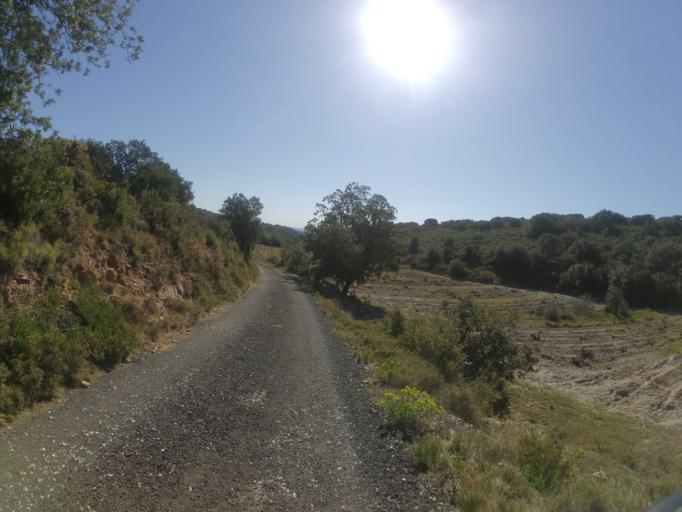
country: FR
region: Languedoc-Roussillon
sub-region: Departement des Pyrenees-Orientales
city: Baixas
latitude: 42.7612
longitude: 2.7816
